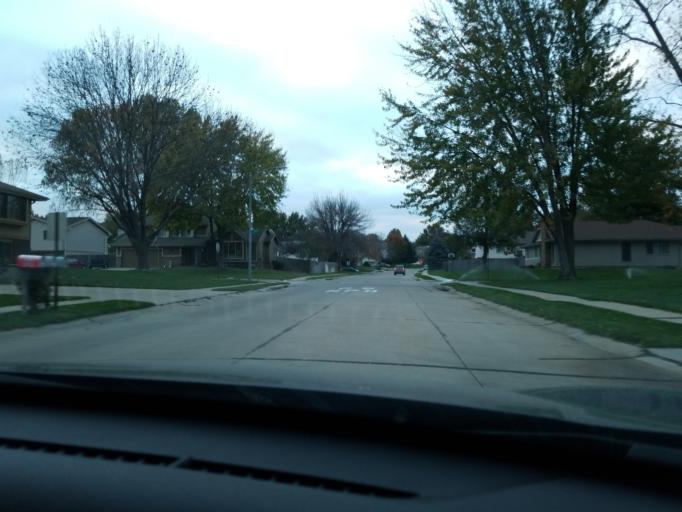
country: US
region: Nebraska
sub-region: Sarpy County
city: La Vista
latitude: 41.1713
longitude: -96.0293
